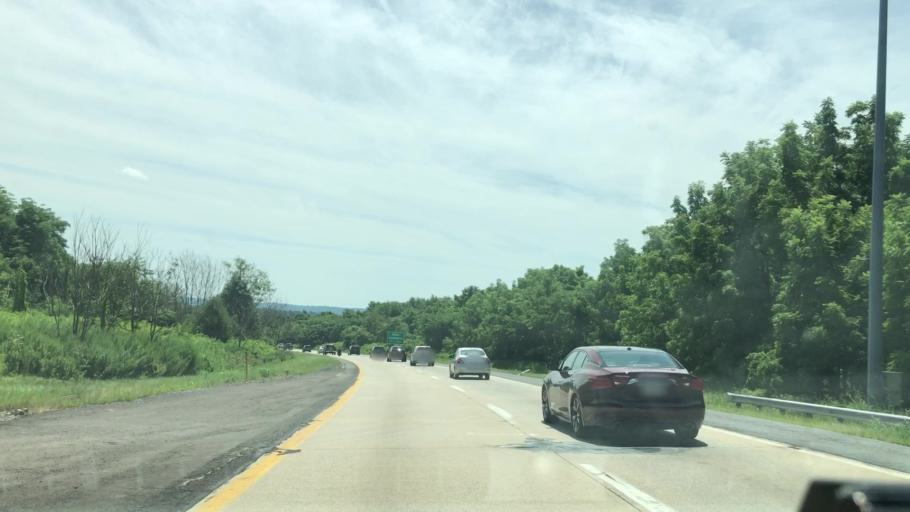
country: US
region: Pennsylvania
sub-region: Montgomery County
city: Audubon
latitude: 40.1479
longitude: -75.4603
